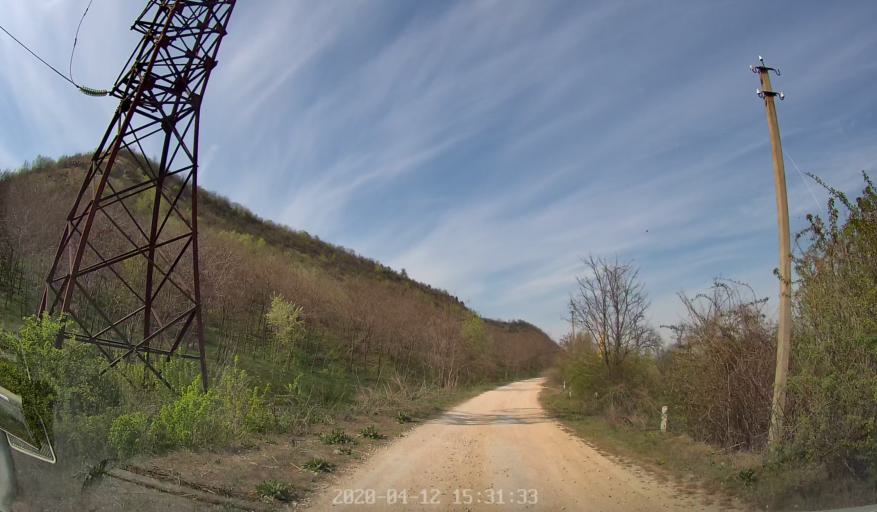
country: MD
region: Telenesti
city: Cocieri
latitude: 47.3238
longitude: 29.0740
